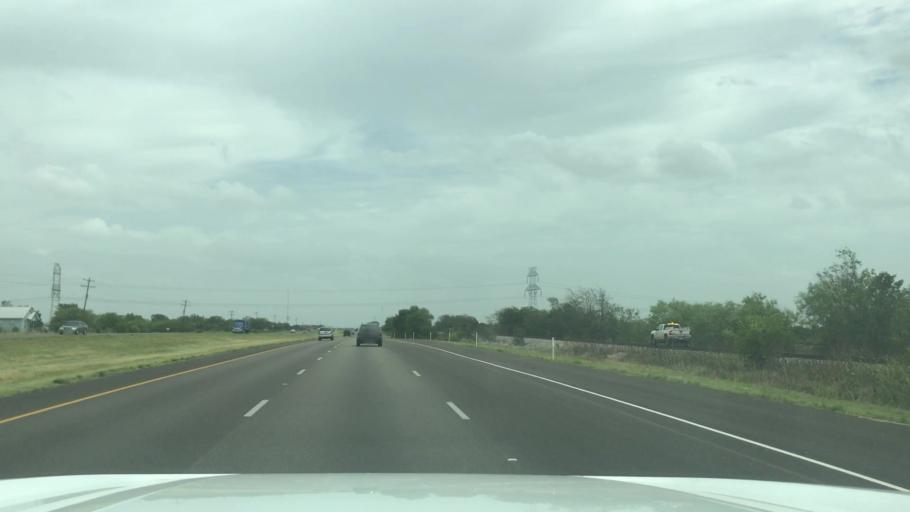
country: US
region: Texas
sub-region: McLennan County
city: Riesel
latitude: 31.5203
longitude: -96.9853
